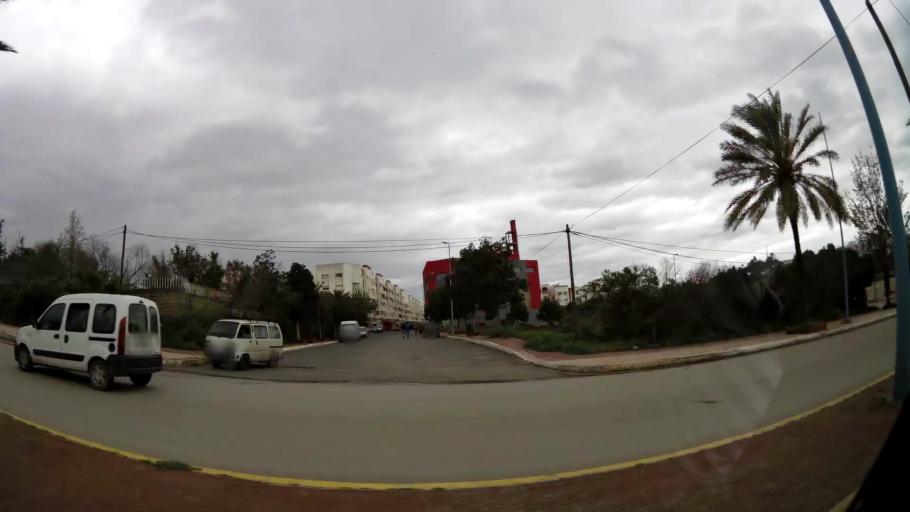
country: MA
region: Grand Casablanca
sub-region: Mediouna
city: Tit Mellil
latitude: 33.5578
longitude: -7.5378
